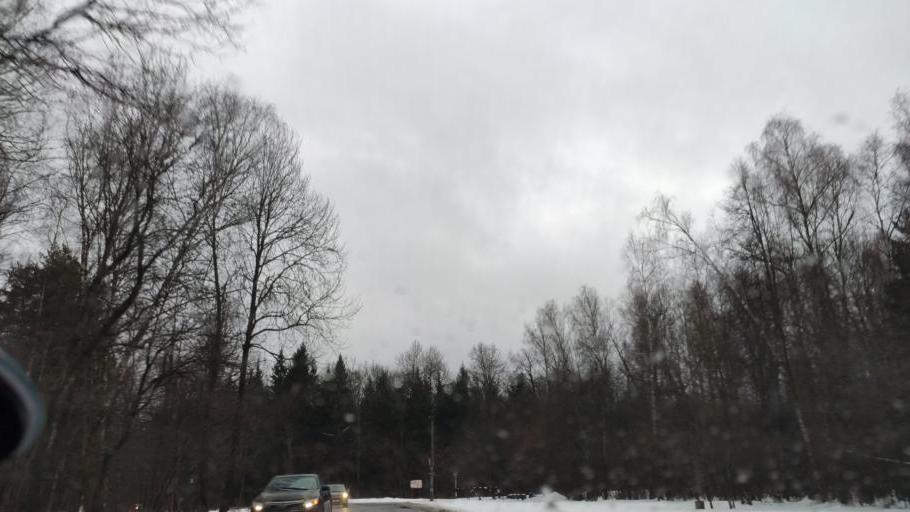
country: RU
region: Moskovskaya
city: Vatutinki
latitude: 55.4830
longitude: 37.3352
